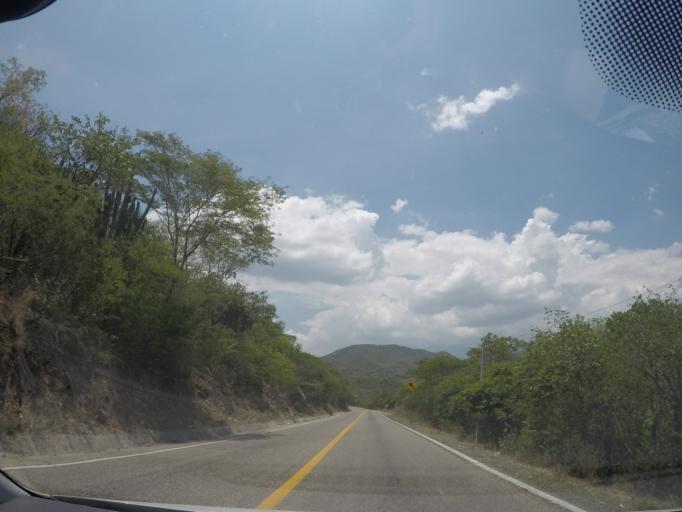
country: MX
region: Oaxaca
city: Asuncion Tlacolulita
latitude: 16.3997
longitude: -95.7730
